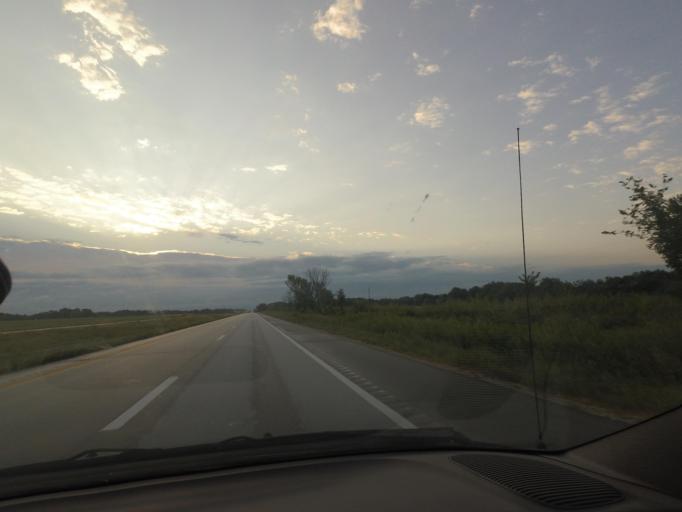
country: US
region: Missouri
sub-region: Shelby County
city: Shelbina
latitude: 39.7260
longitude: -92.1784
